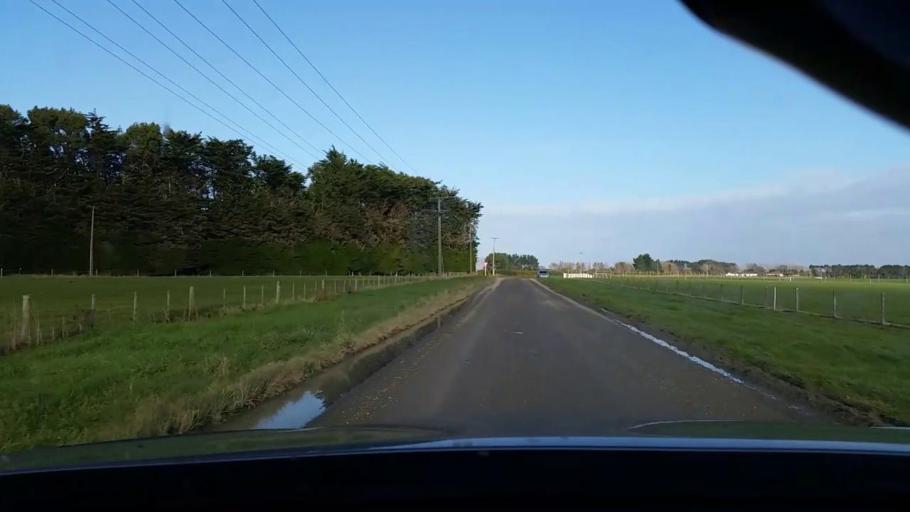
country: NZ
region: Southland
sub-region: Invercargill City
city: Invercargill
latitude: -46.3085
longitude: 168.3034
